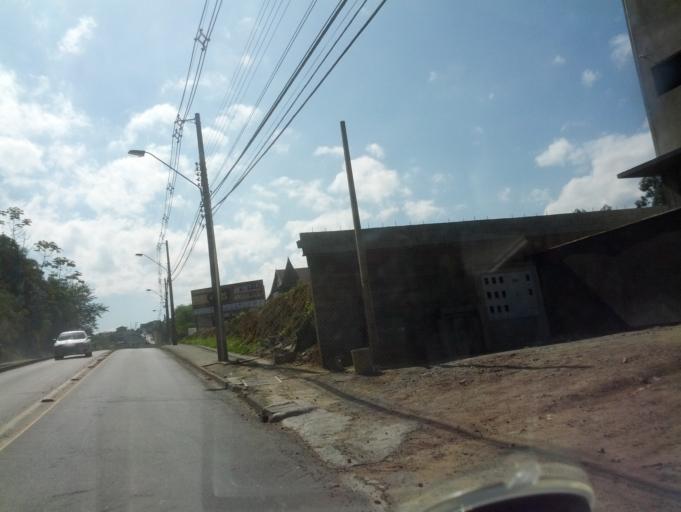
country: BR
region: Santa Catarina
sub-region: Blumenau
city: Blumenau
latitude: -26.8832
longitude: -49.0626
